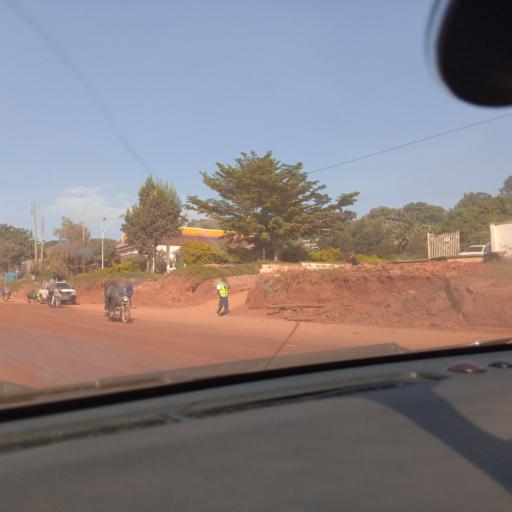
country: UG
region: Central Region
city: Masaka
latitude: -0.3387
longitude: 31.7388
